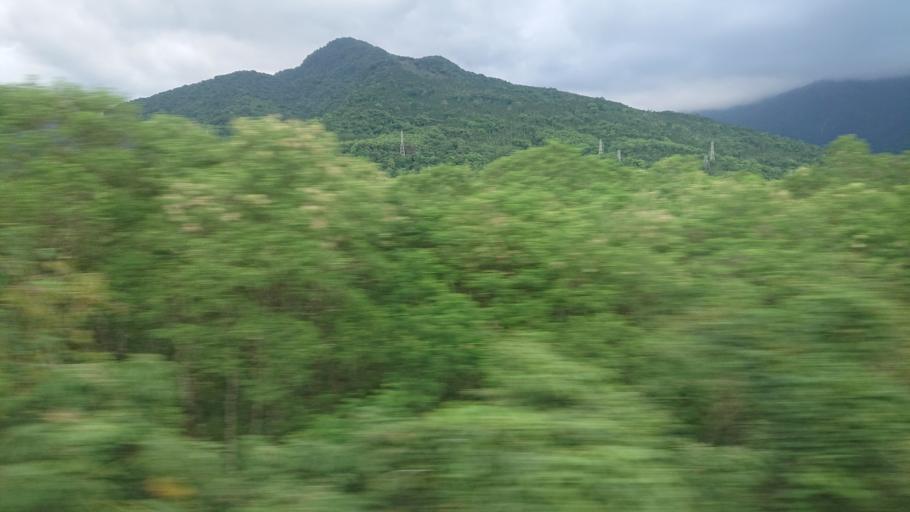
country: TW
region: Taiwan
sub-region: Hualien
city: Hualian
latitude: 23.6202
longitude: 121.3957
